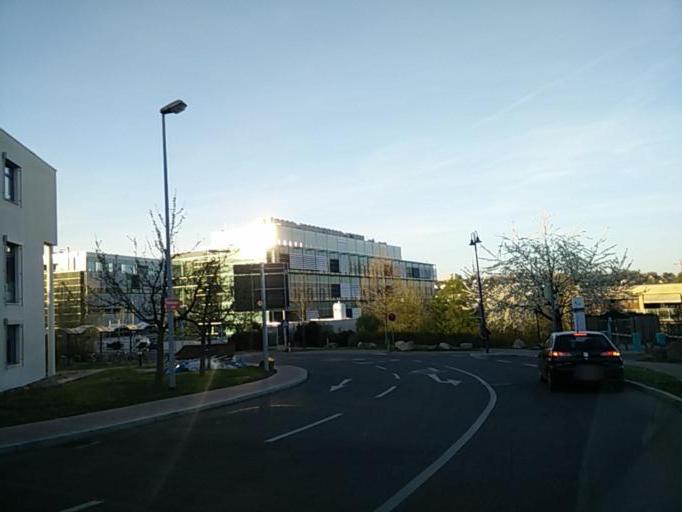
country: DE
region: Baden-Wuerttemberg
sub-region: Tuebingen Region
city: Tuebingen
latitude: 48.5306
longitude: 9.0412
